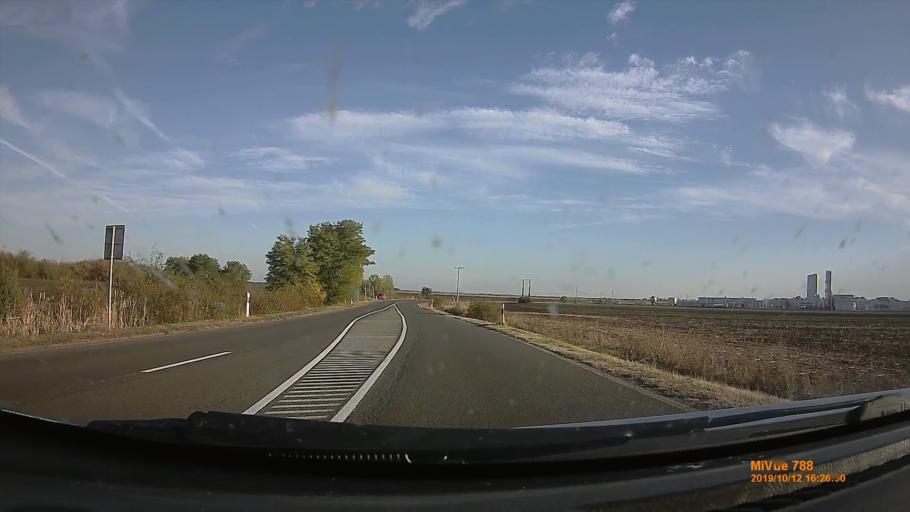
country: HU
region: Heves
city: Gyongyoshalasz
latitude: 47.7295
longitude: 19.9606
